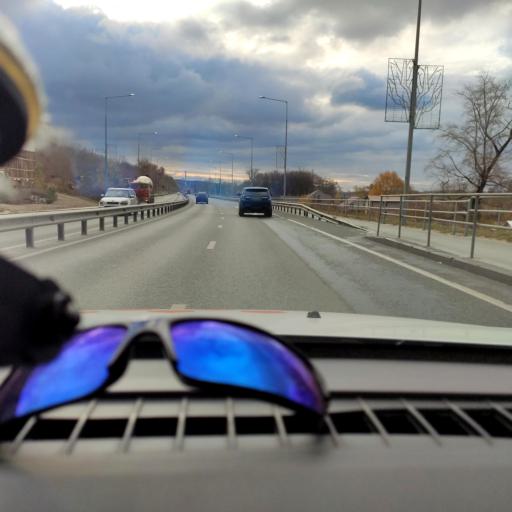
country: RU
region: Samara
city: Volzhskiy
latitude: 53.3977
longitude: 50.1508
